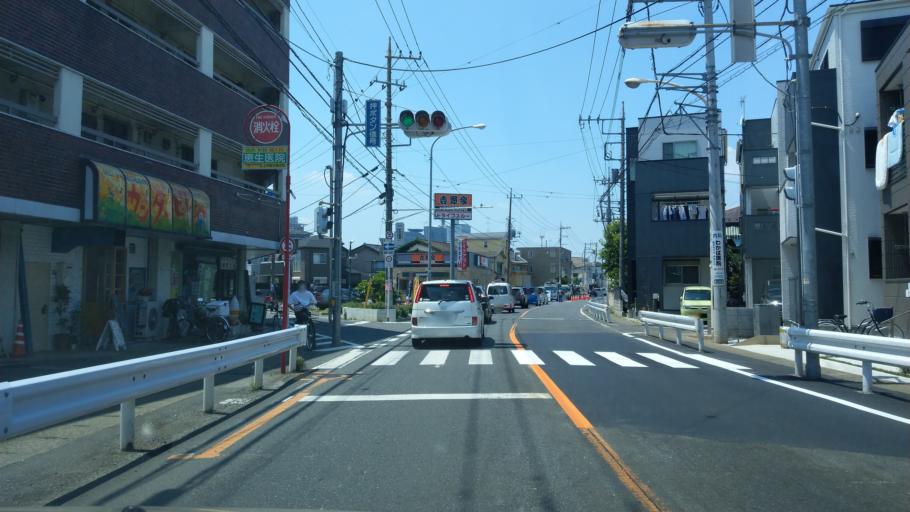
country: JP
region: Saitama
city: Yono
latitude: 35.8839
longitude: 139.6497
